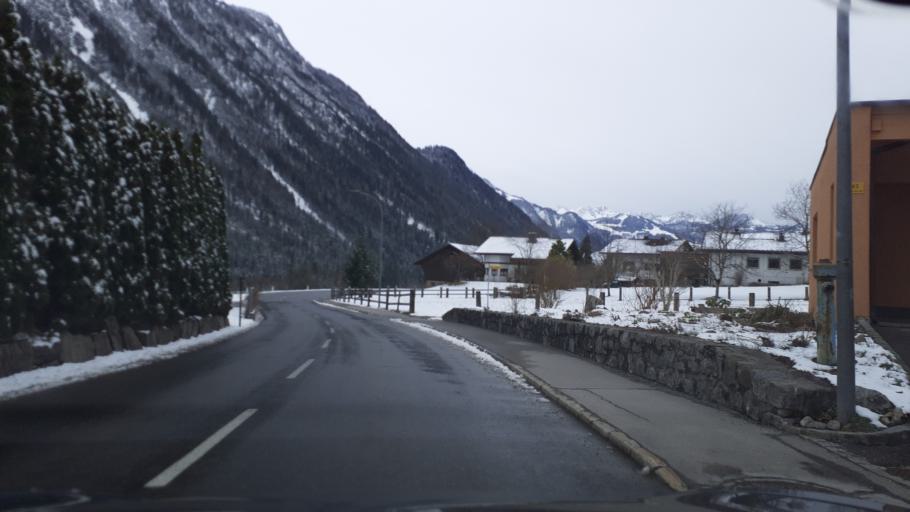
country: AT
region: Vorarlberg
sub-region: Politischer Bezirk Bludenz
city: Innerbraz
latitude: 47.1455
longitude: 9.9142
